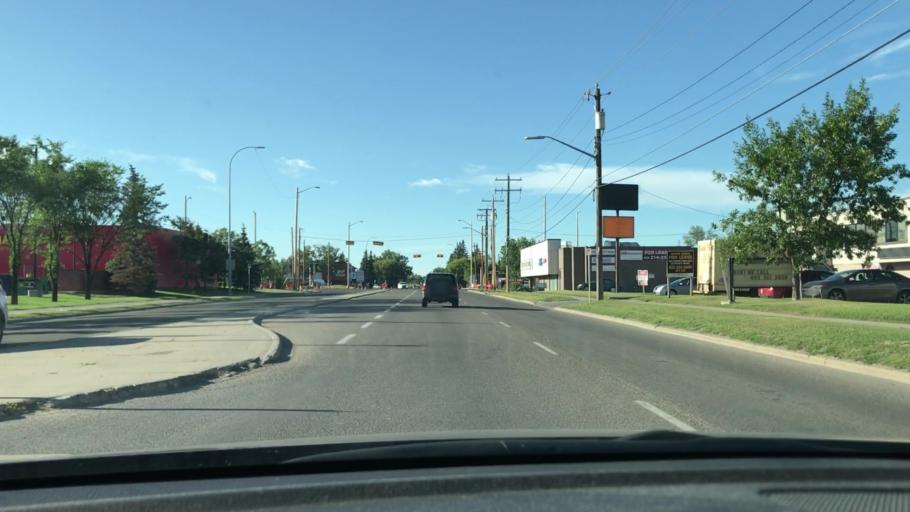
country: CA
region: Alberta
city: Calgary
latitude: 51.0364
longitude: -113.9583
